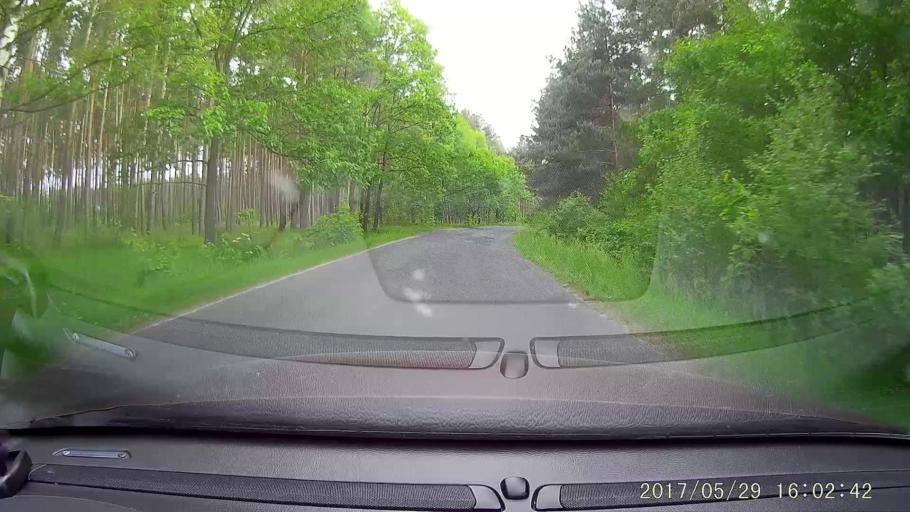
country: PL
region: Lower Silesian Voivodeship
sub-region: Powiat zgorzelecki
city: Wegliniec
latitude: 51.2262
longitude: 15.2079
